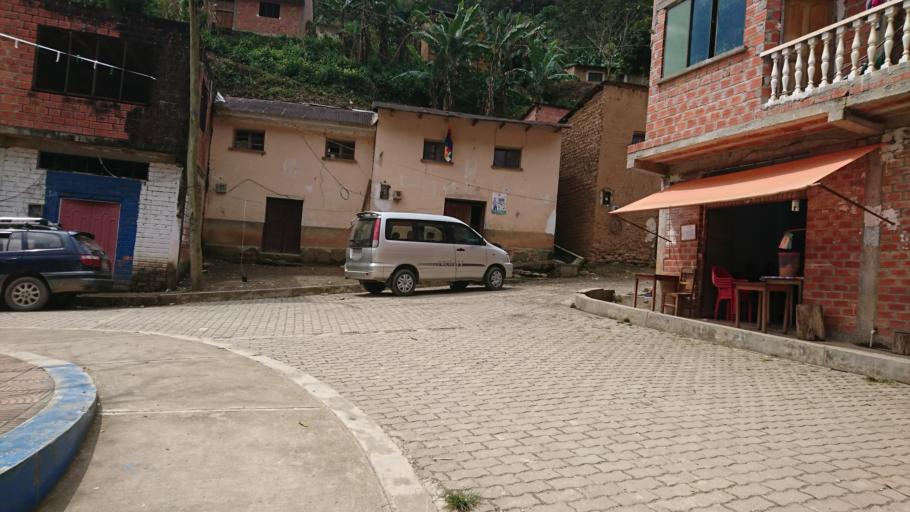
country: BO
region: La Paz
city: Coroico
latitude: -16.0381
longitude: -67.8177
